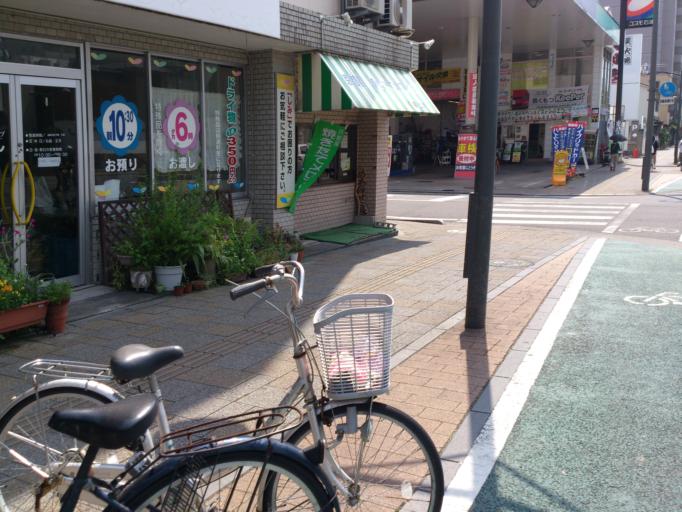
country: JP
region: Ehime
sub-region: Shikoku-chuo Shi
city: Matsuyama
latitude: 33.8474
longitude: 132.7688
